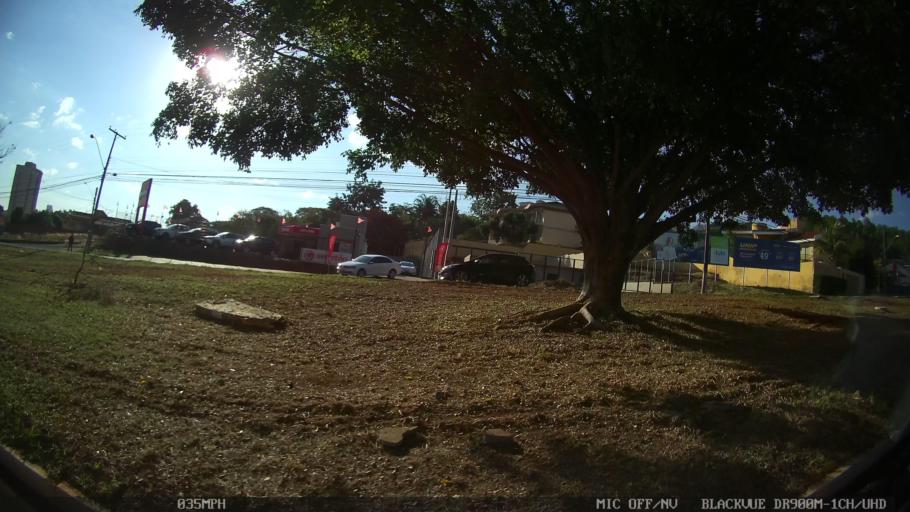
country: BR
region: Sao Paulo
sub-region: Ribeirao Preto
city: Ribeirao Preto
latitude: -21.2067
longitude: -47.7870
